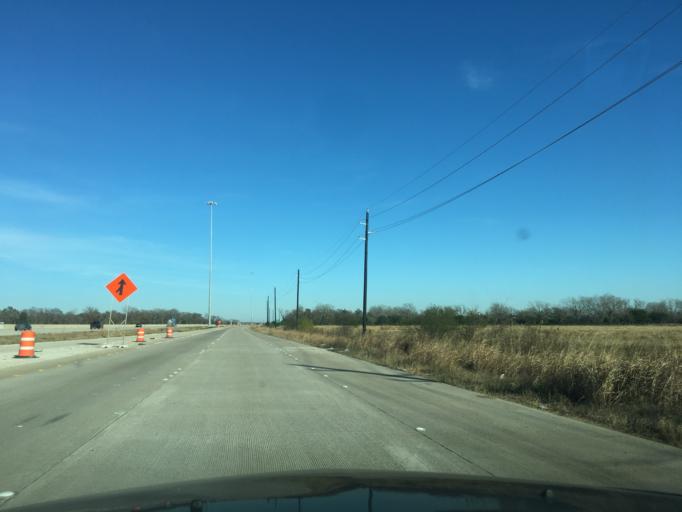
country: US
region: Texas
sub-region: Fort Bend County
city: Richmond
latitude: 29.5503
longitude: -95.7370
